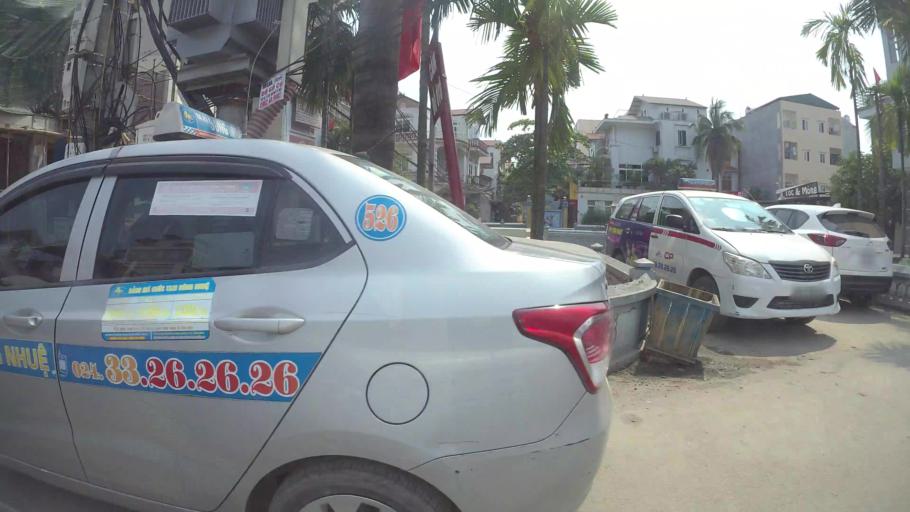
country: VN
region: Ha Noi
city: Ha Dong
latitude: 20.9898
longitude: 105.7732
